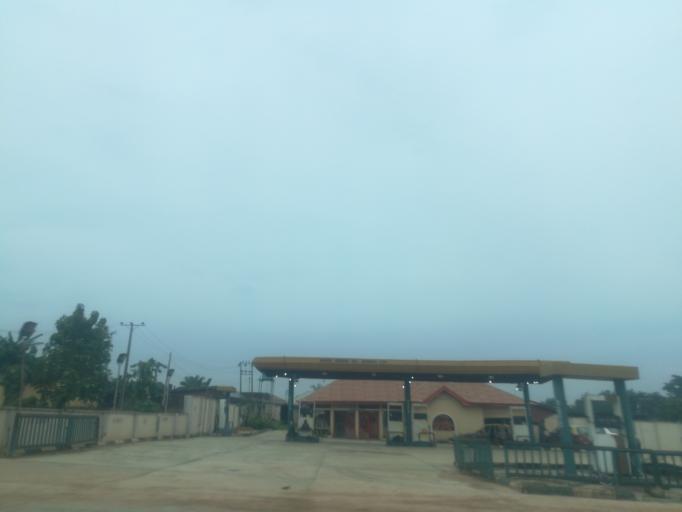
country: NG
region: Oyo
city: Egbeda
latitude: 7.3818
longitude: 4.0047
